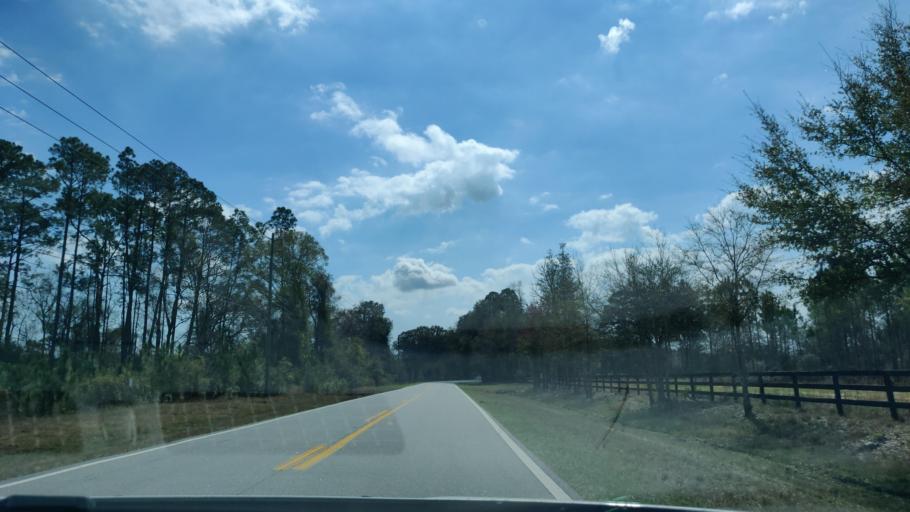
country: US
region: Florida
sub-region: Duval County
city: Baldwin
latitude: 30.2566
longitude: -81.9505
